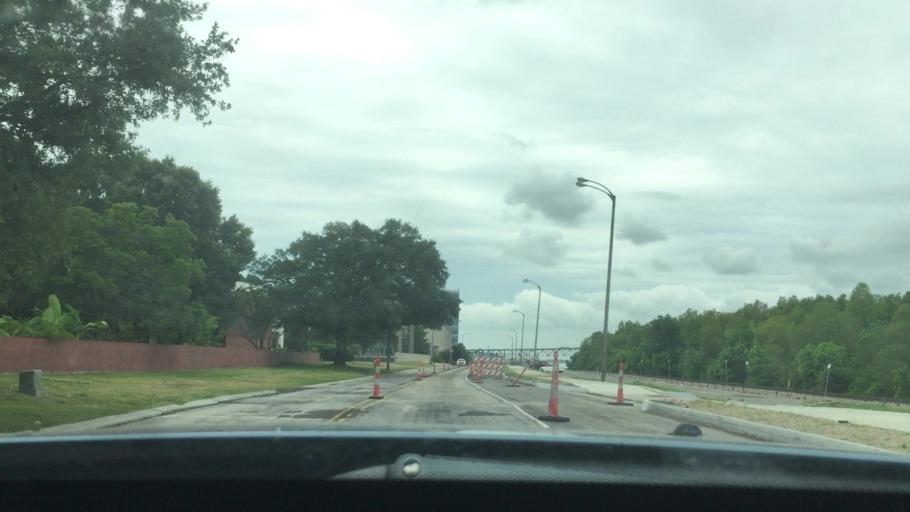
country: US
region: Louisiana
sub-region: West Baton Rouge Parish
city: Port Allen
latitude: 30.4561
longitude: -91.1900
